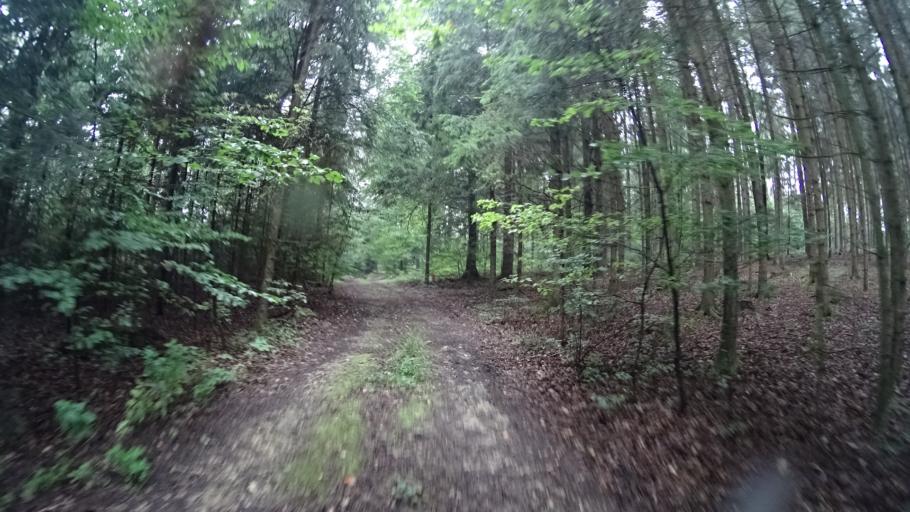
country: DE
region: Bavaria
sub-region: Upper Bavaria
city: Bohmfeld
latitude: 48.9126
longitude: 11.3887
